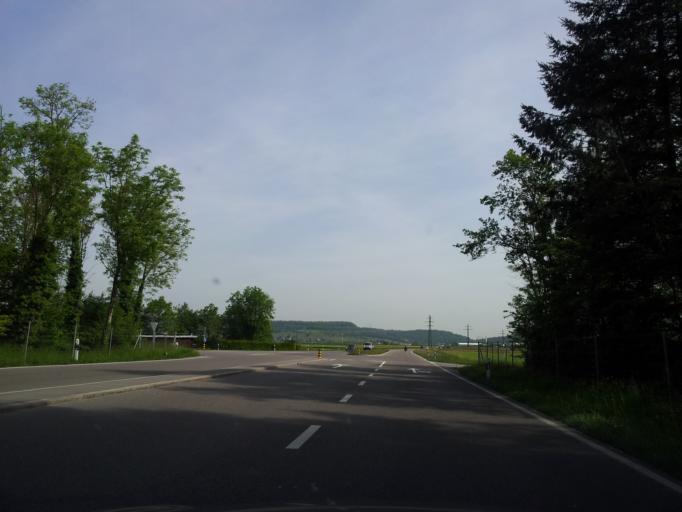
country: CH
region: Zurich
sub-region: Bezirk Buelach
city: Seglingen
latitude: 47.5903
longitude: 8.5286
